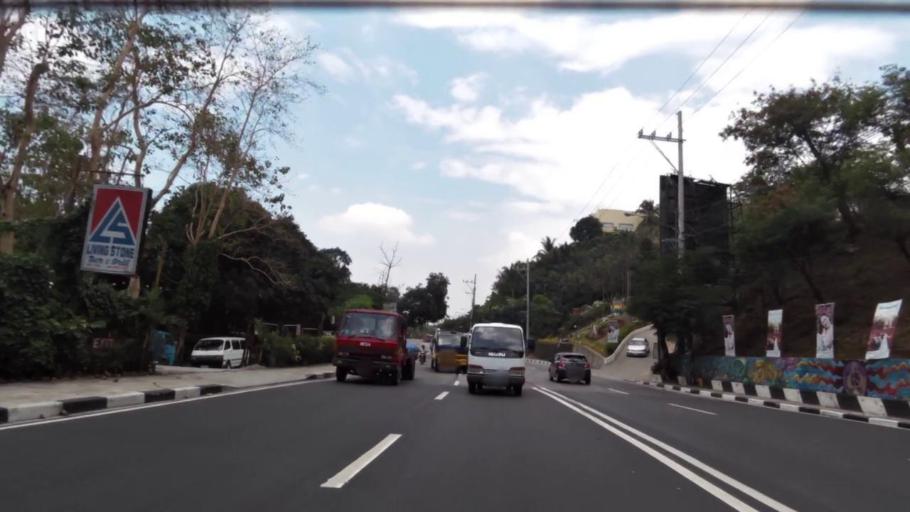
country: PH
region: Calabarzon
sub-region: Province of Rizal
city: Antipolo
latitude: 14.6130
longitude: 121.1559
